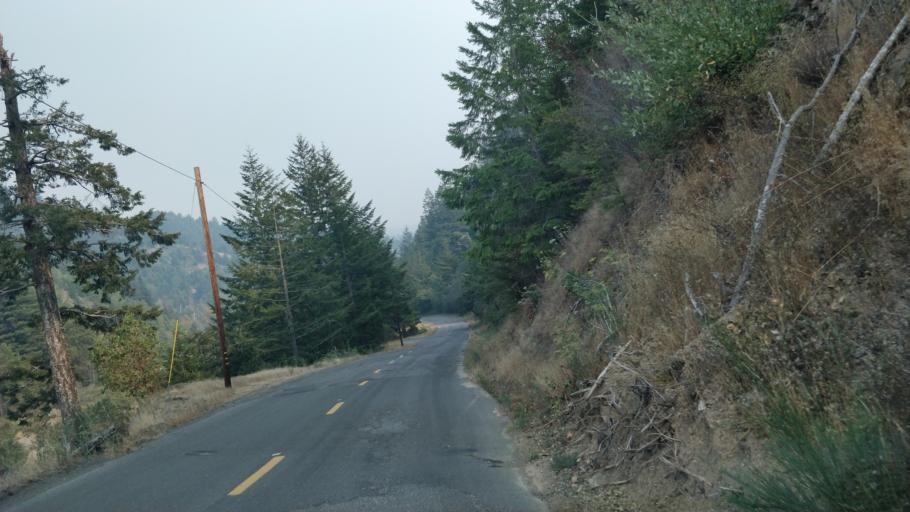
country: US
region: California
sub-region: Humboldt County
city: Rio Dell
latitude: 40.3107
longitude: -124.2696
